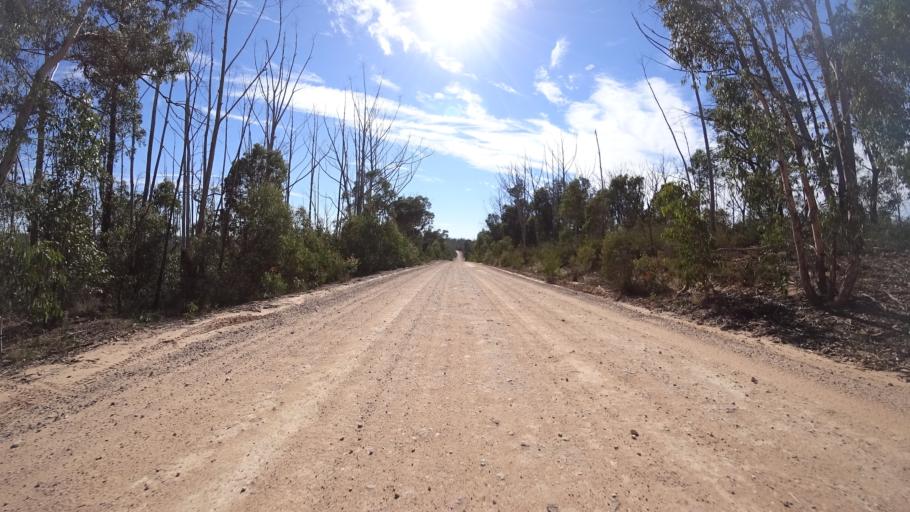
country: AU
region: New South Wales
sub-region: Lithgow
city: Lithgow
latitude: -33.4337
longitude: 150.1875
